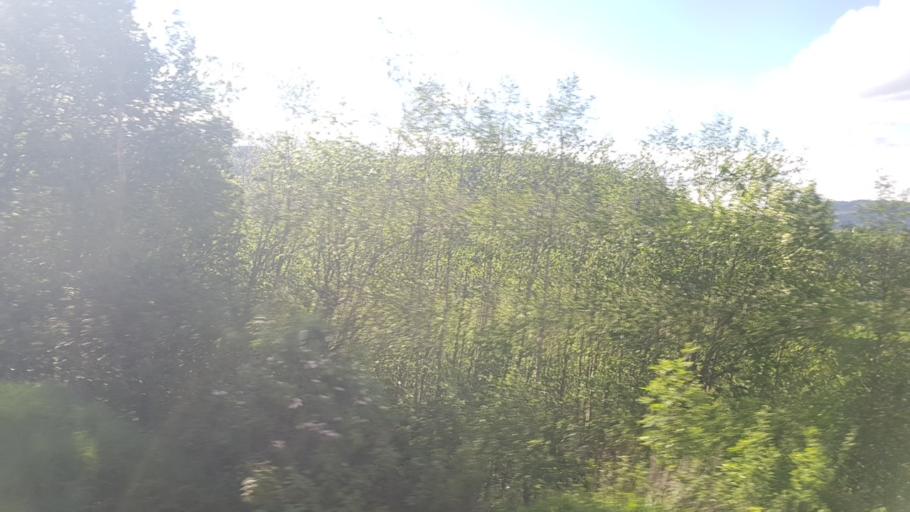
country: NO
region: Sor-Trondelag
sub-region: Midtre Gauldal
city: Storen
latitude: 62.9675
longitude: 10.1993
